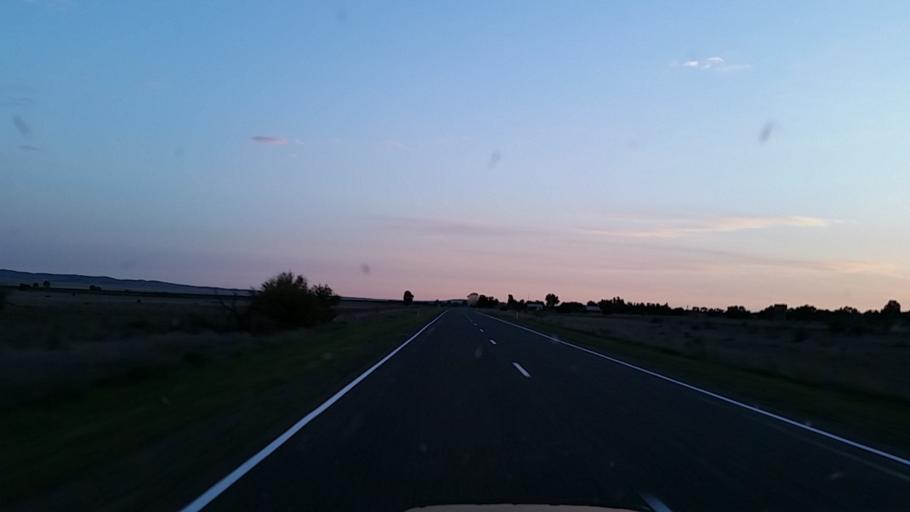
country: AU
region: South Australia
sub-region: Peterborough
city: Peterborough
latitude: -33.1474
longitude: 138.9264
